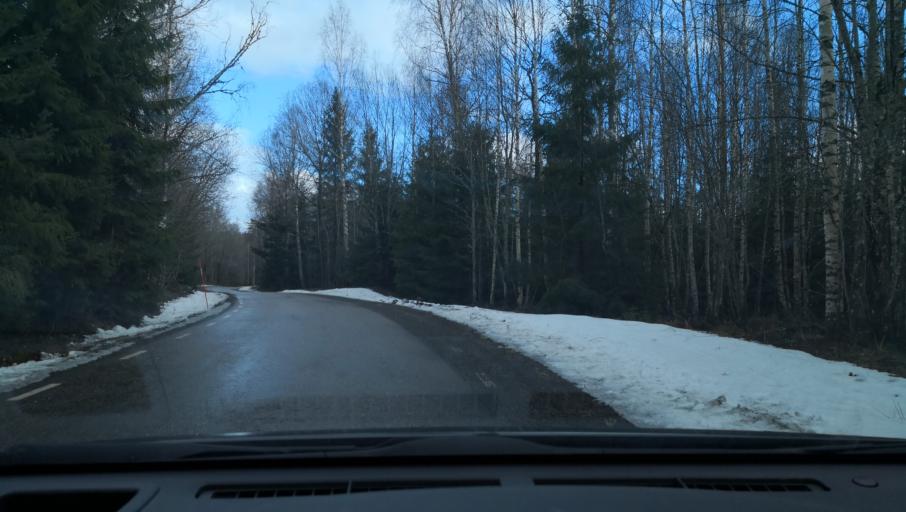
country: SE
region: Vaestmanland
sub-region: Arboga Kommun
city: Arboga
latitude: 59.3365
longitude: 15.7093
